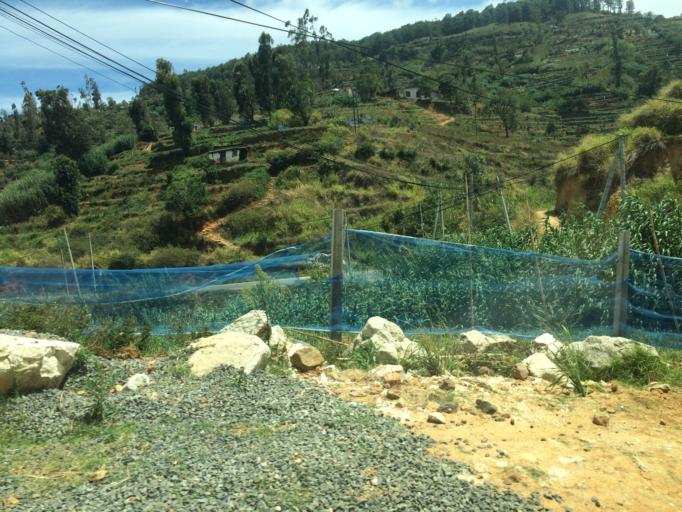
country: LK
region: Central
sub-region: Nuwara Eliya District
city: Nuwara Eliya
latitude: 6.9080
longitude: 80.8380
